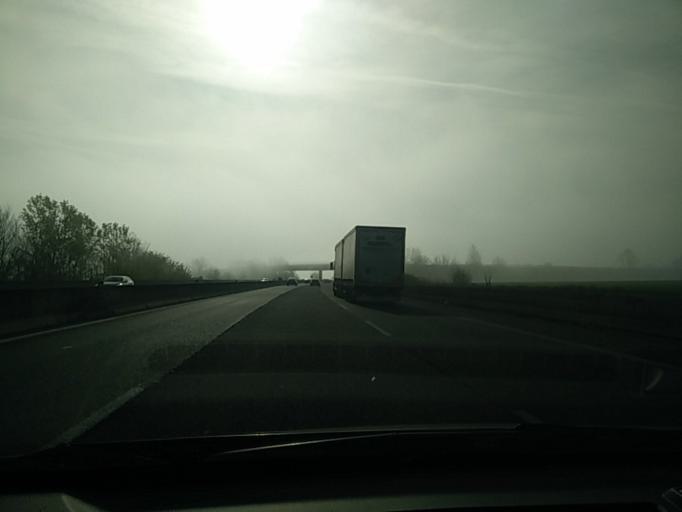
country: IT
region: Emilia-Romagna
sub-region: Provincia di Bologna
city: Osteria Grande
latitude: 44.4541
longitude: 11.5327
